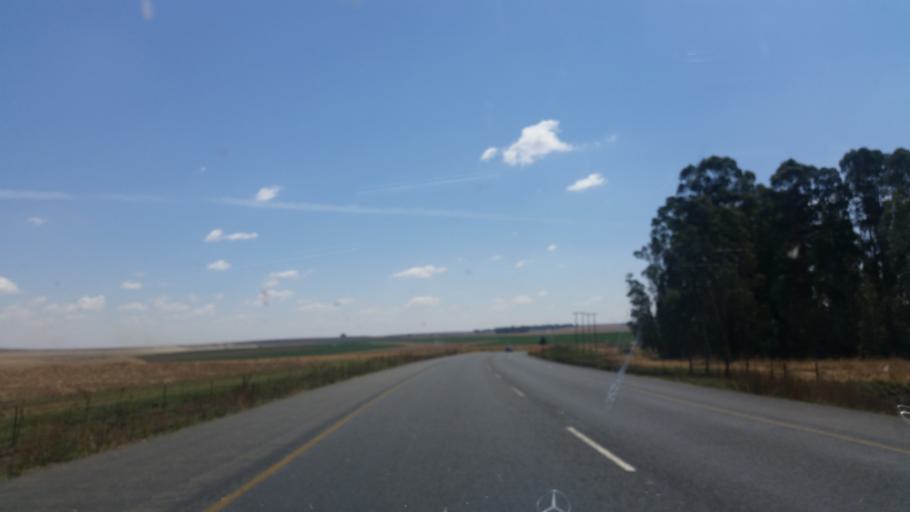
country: ZA
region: Orange Free State
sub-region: Thabo Mofutsanyana District Municipality
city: Bethlehem
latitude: -28.1046
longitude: 28.6610
